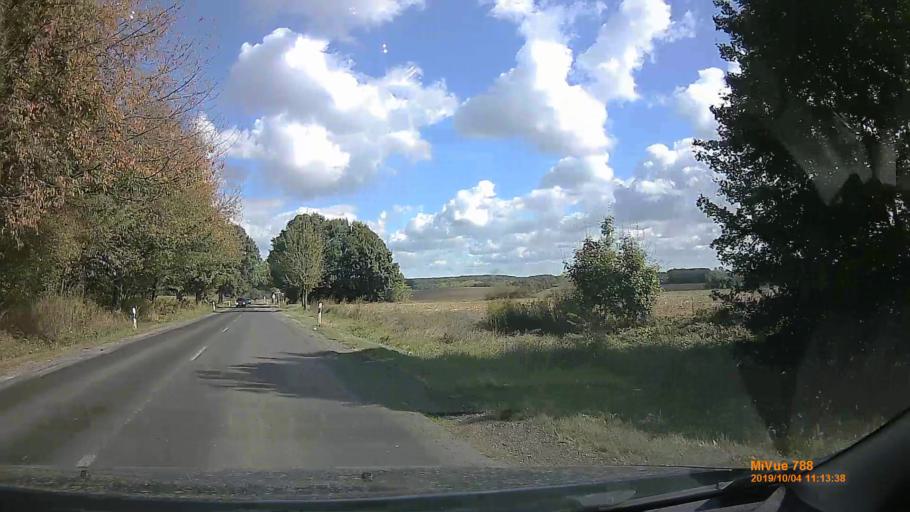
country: HU
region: Somogy
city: Kaposvar
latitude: 46.4309
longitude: 17.7831
